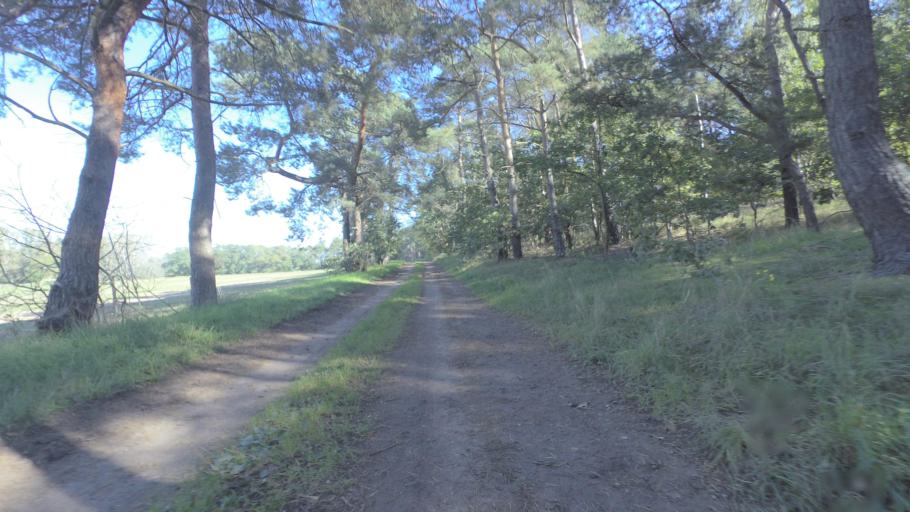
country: DE
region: Brandenburg
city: Rangsdorf
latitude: 52.2800
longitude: 13.3528
